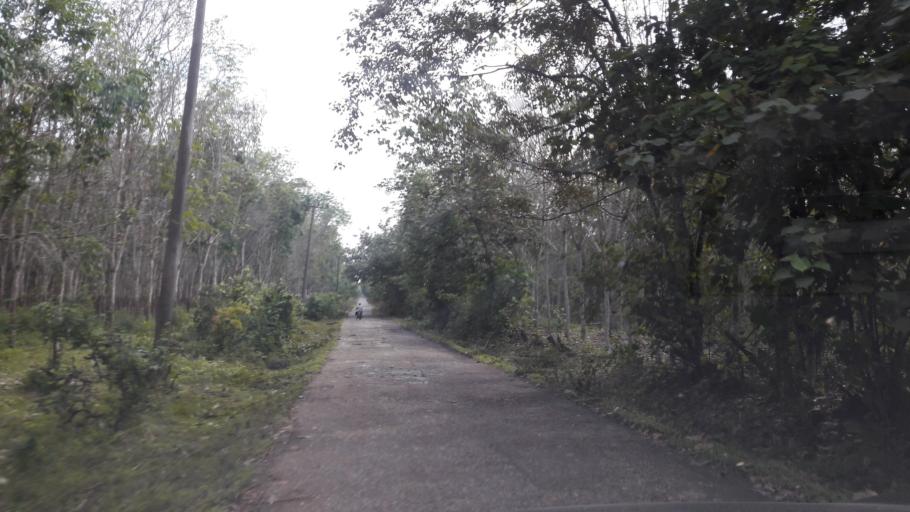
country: ID
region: South Sumatra
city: Gunungmenang
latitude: -3.1033
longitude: 104.0652
